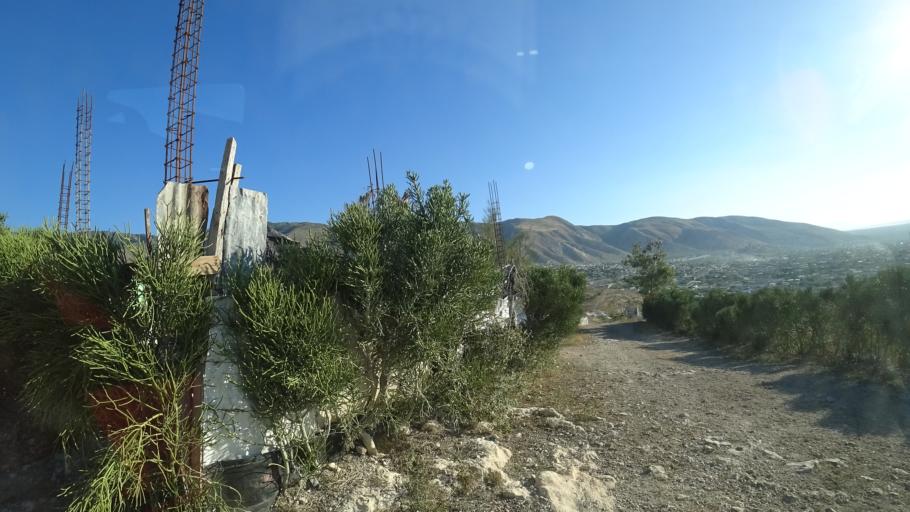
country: HT
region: Ouest
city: Croix des Bouquets
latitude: 18.6707
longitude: -72.2463
